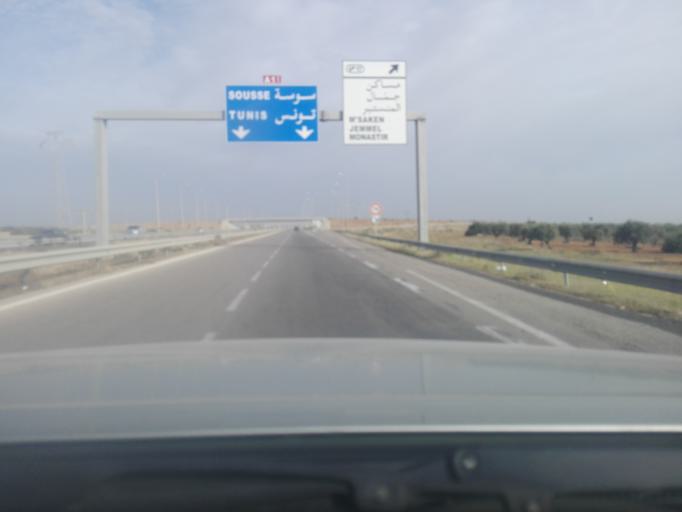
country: TN
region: Al Munastir
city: Manzil Kamil
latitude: 35.6392
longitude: 10.5803
